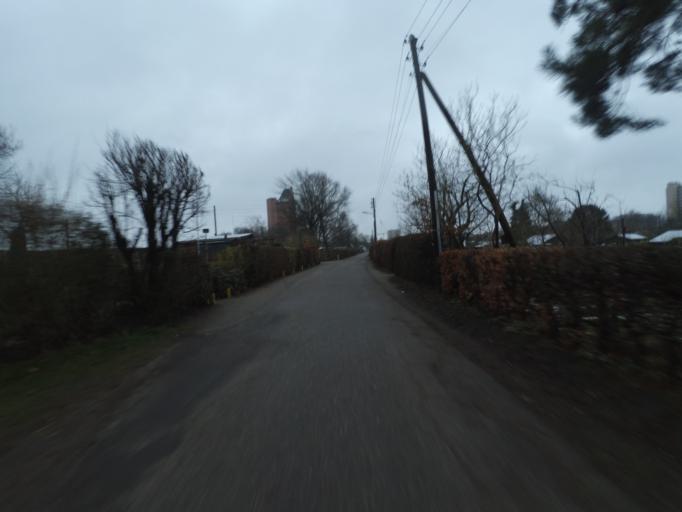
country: DE
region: Hamburg
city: Stellingen
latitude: 53.5875
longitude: 9.9370
